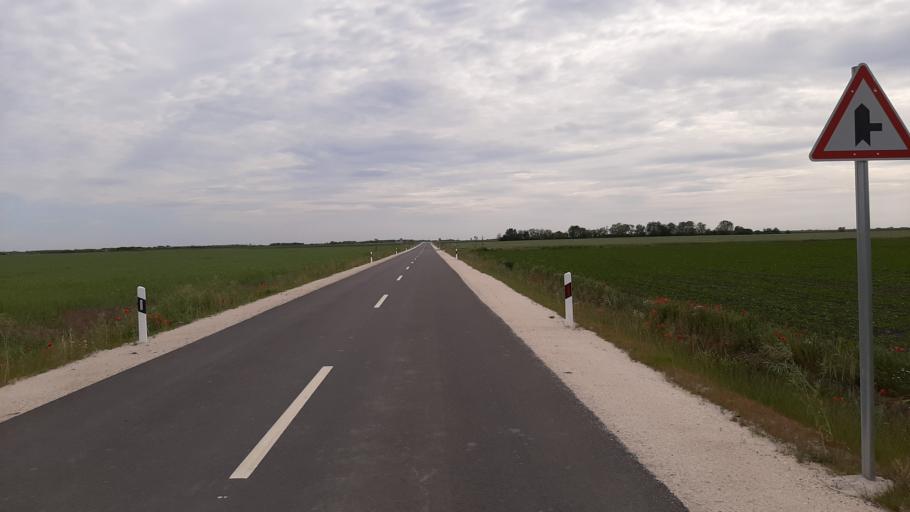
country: RO
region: Timis
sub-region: Comuna Beba Veche
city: Beba Veche
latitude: 46.1403
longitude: 20.2756
